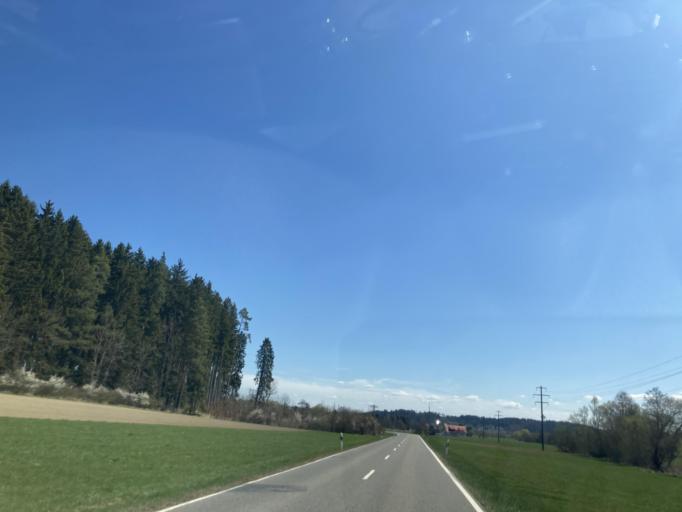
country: DE
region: Baden-Wuerttemberg
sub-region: Freiburg Region
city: Villingen-Schwenningen
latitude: 48.0305
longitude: 8.4390
